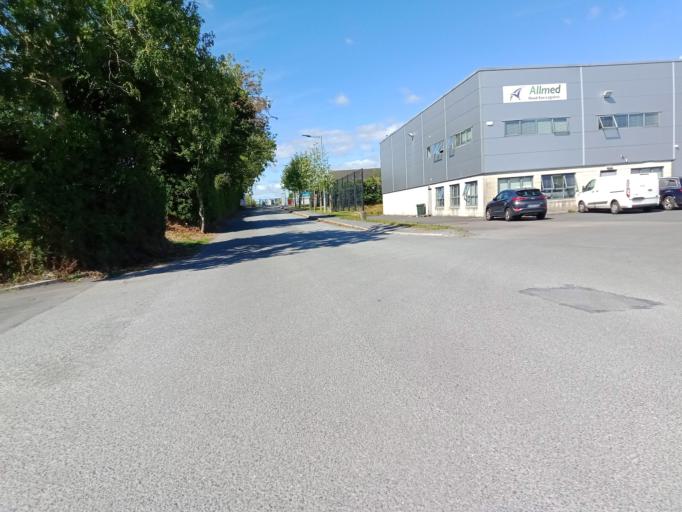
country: IE
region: Leinster
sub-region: Kilkenny
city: Thomastown
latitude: 52.5391
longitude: -7.1388
